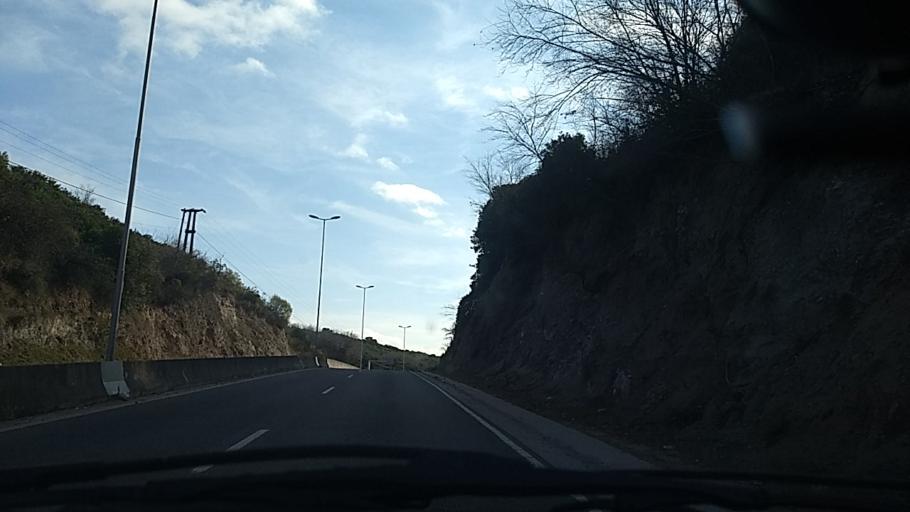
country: AR
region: Cordoba
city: Rio Ceballos
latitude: -31.1591
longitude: -64.3008
